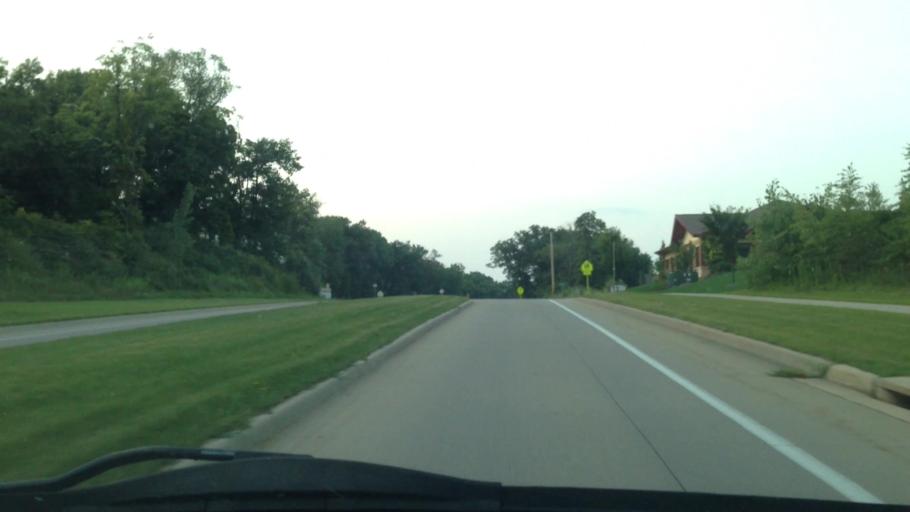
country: US
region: Iowa
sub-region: Johnson County
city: Coralville
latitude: 41.6680
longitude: -91.6036
